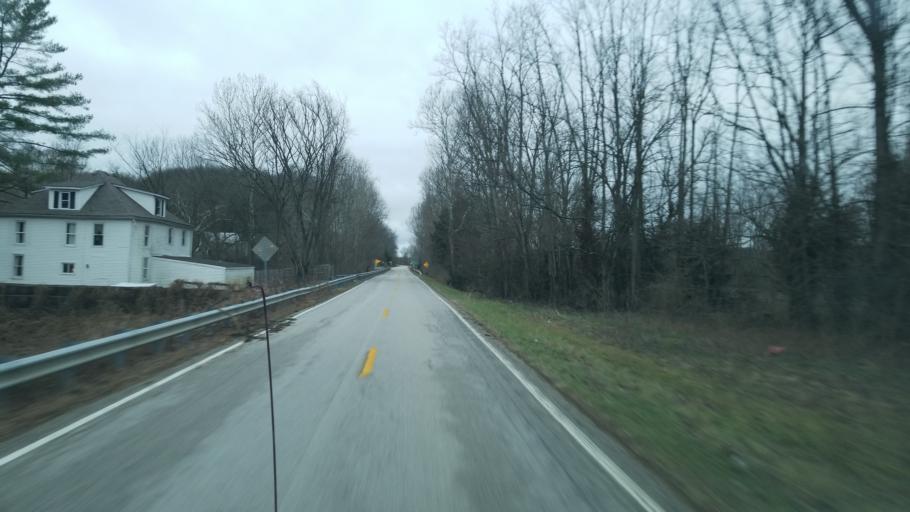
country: US
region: Kentucky
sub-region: Bracken County
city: Brooksville
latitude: 38.7846
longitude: -84.1425
